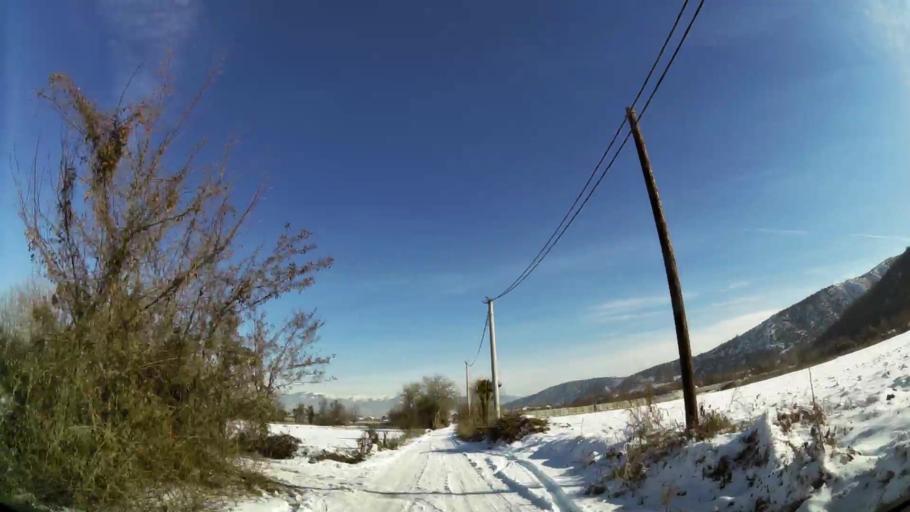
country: MK
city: Grchec
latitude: 41.9827
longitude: 21.3245
